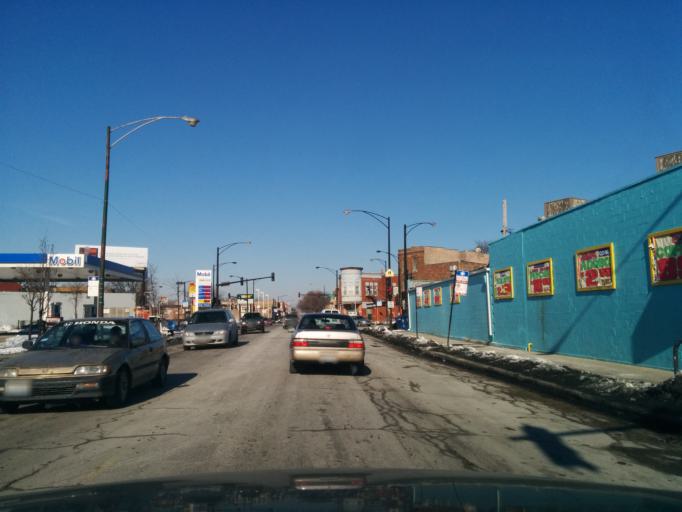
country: US
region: Illinois
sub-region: Cook County
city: Cicero
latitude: 41.9023
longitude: -87.7167
